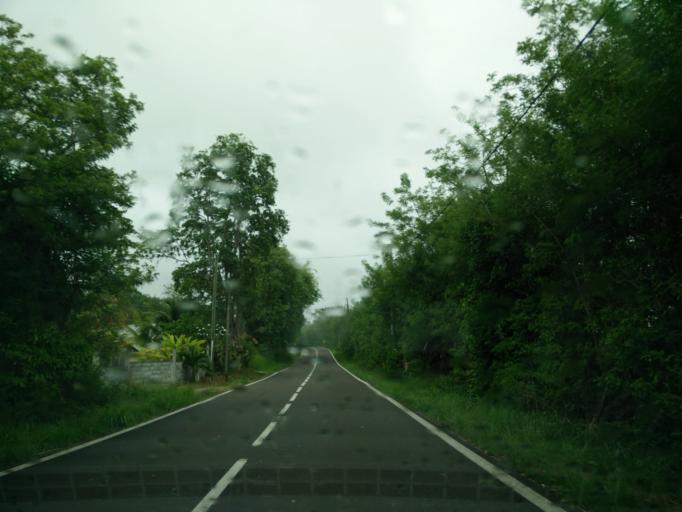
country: GP
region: Guadeloupe
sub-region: Guadeloupe
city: Grand-Bourg
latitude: 15.9009
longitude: -61.2459
